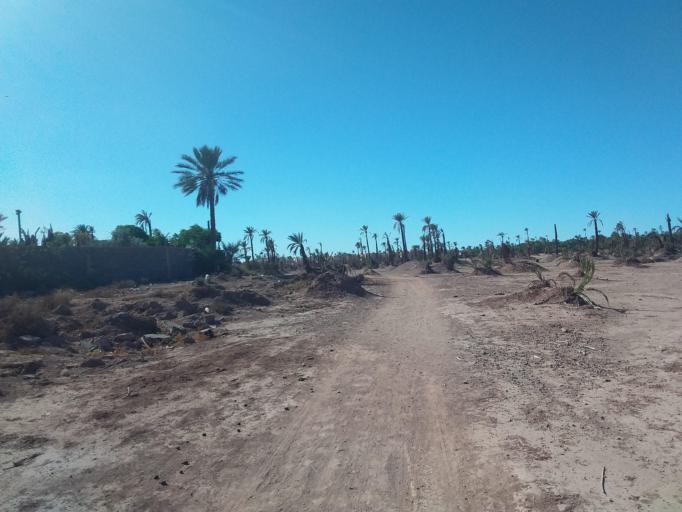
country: MA
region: Marrakech-Tensift-Al Haouz
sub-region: Marrakech
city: Marrakesh
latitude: 31.6800
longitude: -7.9556
